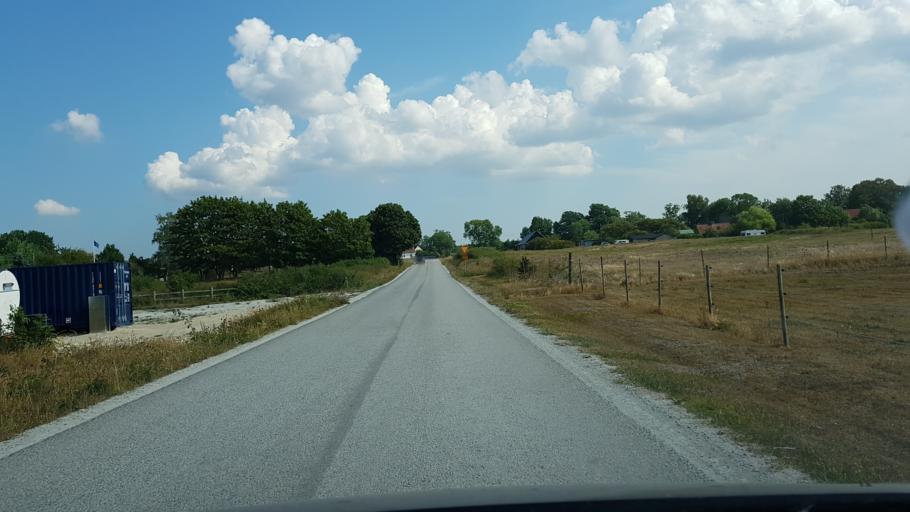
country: SE
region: Gotland
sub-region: Gotland
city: Visby
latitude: 57.8127
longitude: 18.5256
